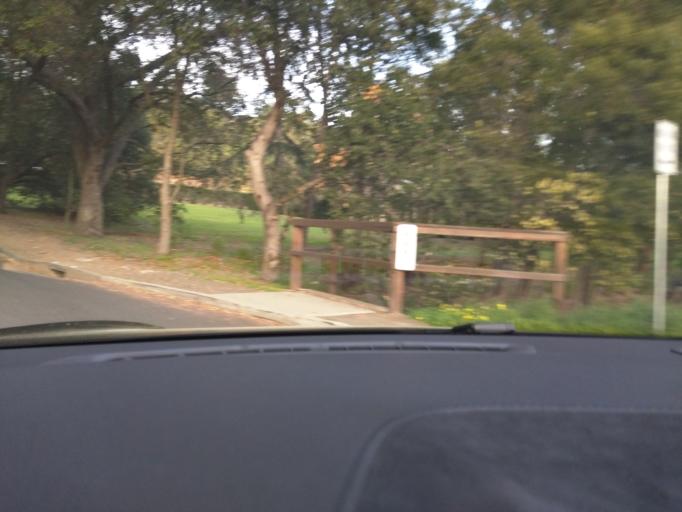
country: US
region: California
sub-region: Santa Clara County
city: Los Altos Hills
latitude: 37.3776
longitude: -122.1471
